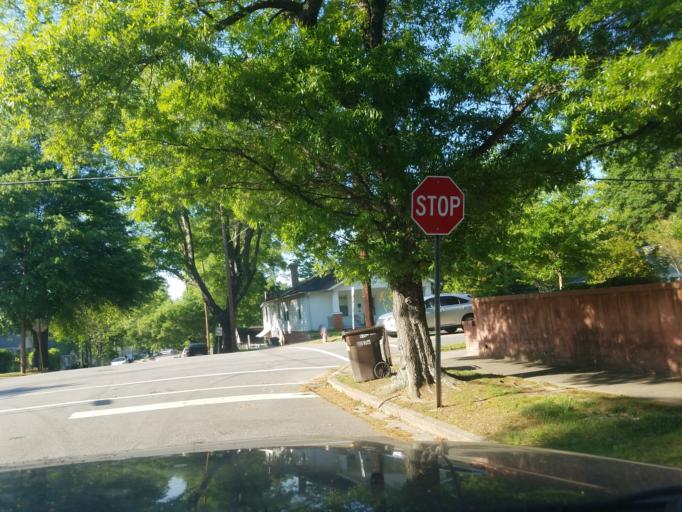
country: US
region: North Carolina
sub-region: Durham County
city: Durham
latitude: 36.0114
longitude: -78.9158
